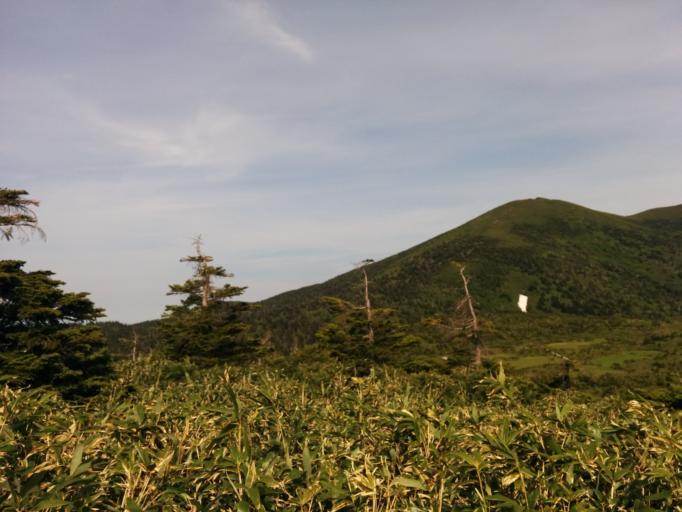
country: JP
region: Aomori
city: Aomori Shi
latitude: 40.6755
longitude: 140.8625
